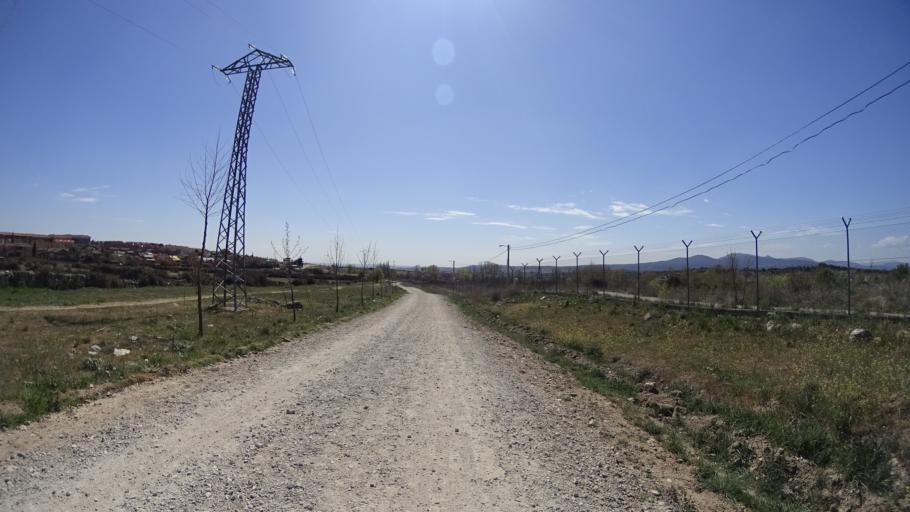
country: ES
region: Madrid
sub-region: Provincia de Madrid
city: Colmenar Viejo
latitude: 40.6758
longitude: -3.7842
